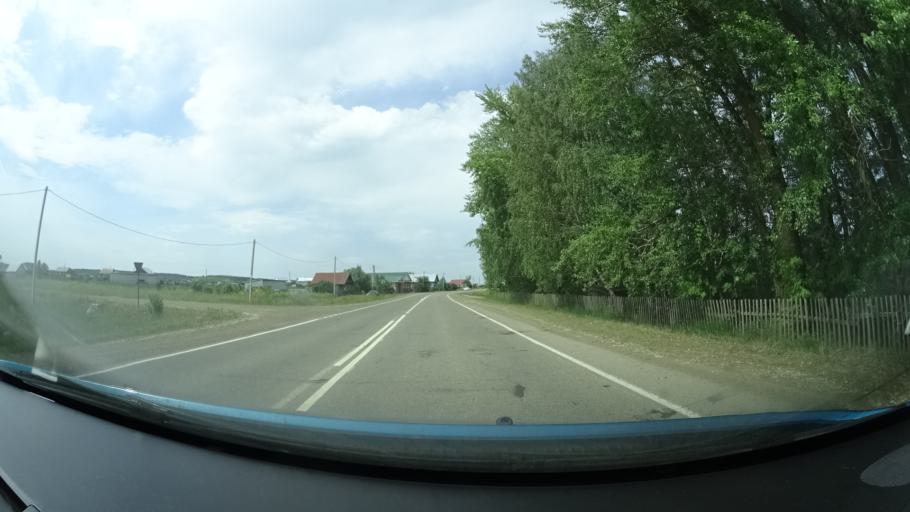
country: RU
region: Perm
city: Barda
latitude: 56.8385
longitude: 55.6150
